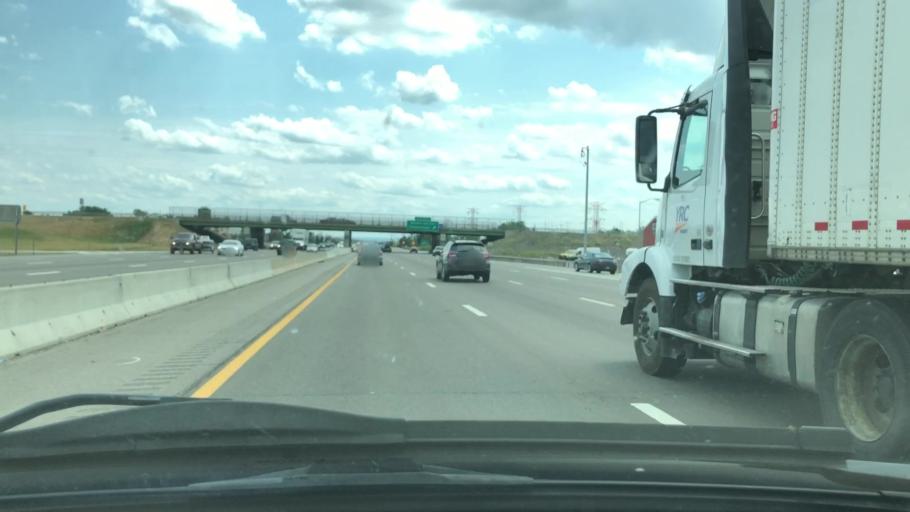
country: US
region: New York
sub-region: Erie County
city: Cheektowaga
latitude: 42.9110
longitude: -78.7677
